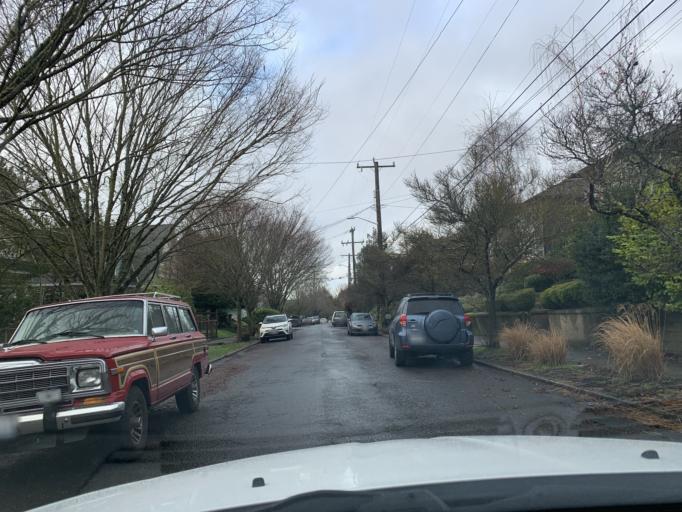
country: US
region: Washington
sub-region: King County
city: Seattle
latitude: 47.6093
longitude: -122.2937
